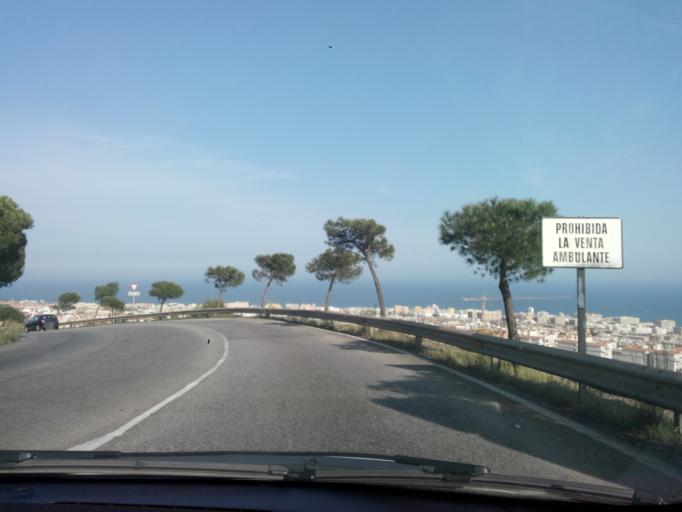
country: ES
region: Andalusia
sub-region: Provincia de Malaga
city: Benalmadena
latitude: 36.6074
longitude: -4.5425
